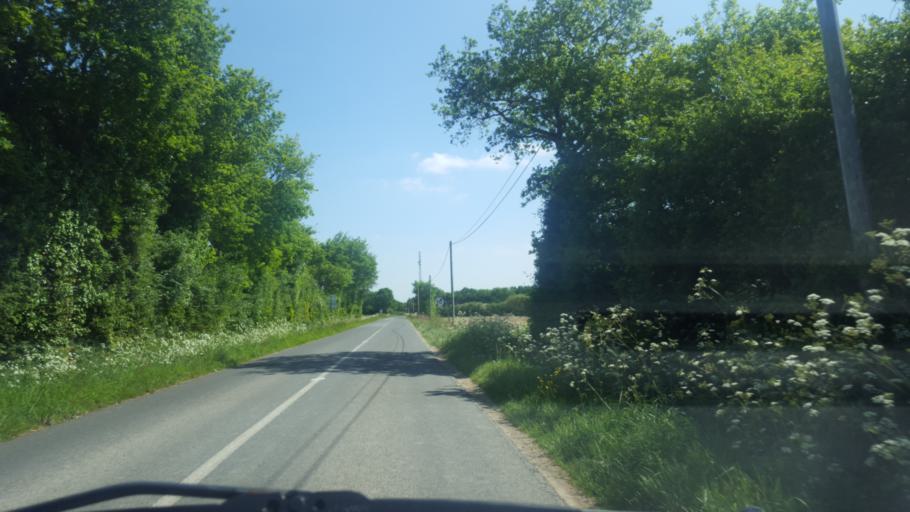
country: FR
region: Pays de la Loire
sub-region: Departement de la Loire-Atlantique
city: La Limouziniere
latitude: 47.0291
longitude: -1.5746
